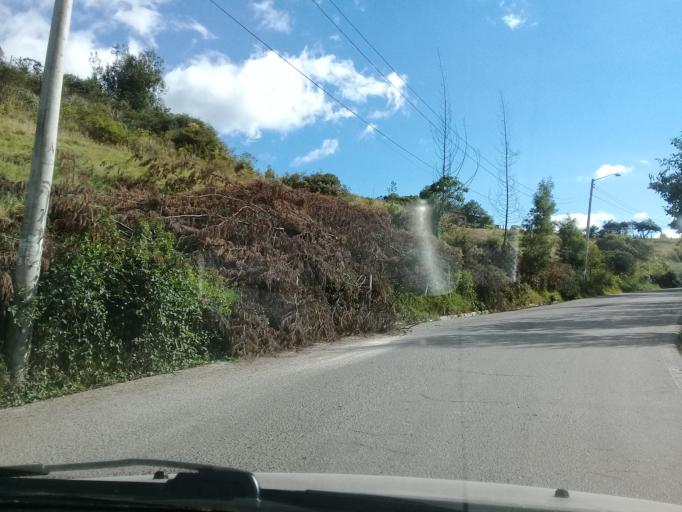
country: CO
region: Cundinamarca
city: Lenguazaque
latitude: 5.3023
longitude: -73.7074
